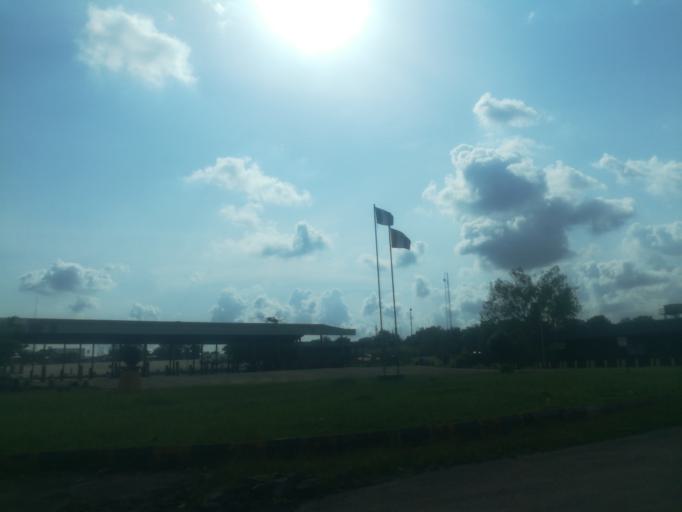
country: NG
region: Oyo
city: Ibadan
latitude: 7.3930
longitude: 3.8197
